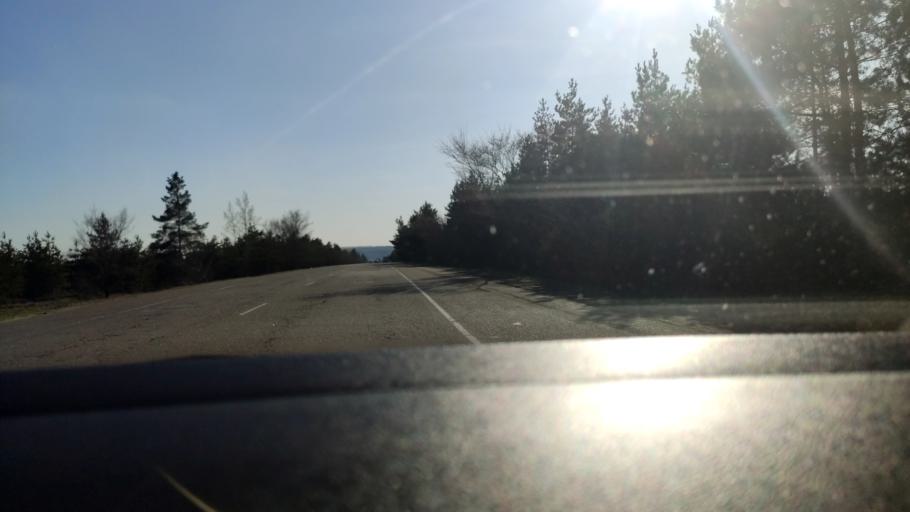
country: RU
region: Voronezj
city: Kolodeznyy
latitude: 51.3643
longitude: 39.1926
